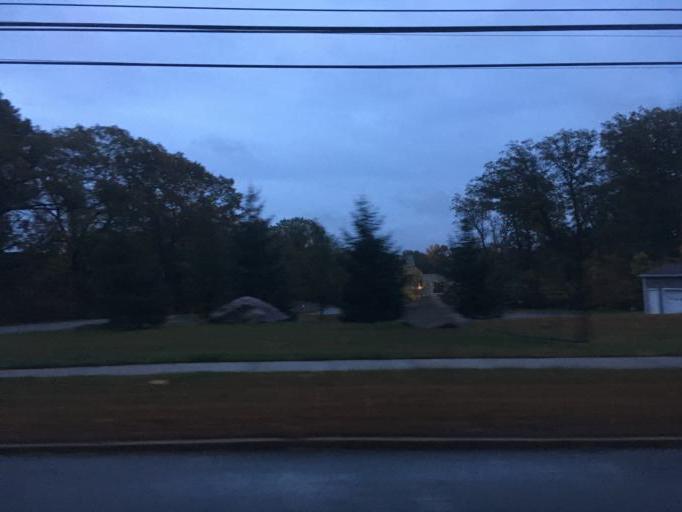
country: US
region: Rhode Island
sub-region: Kent County
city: East Greenwich
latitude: 41.6541
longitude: -71.4970
